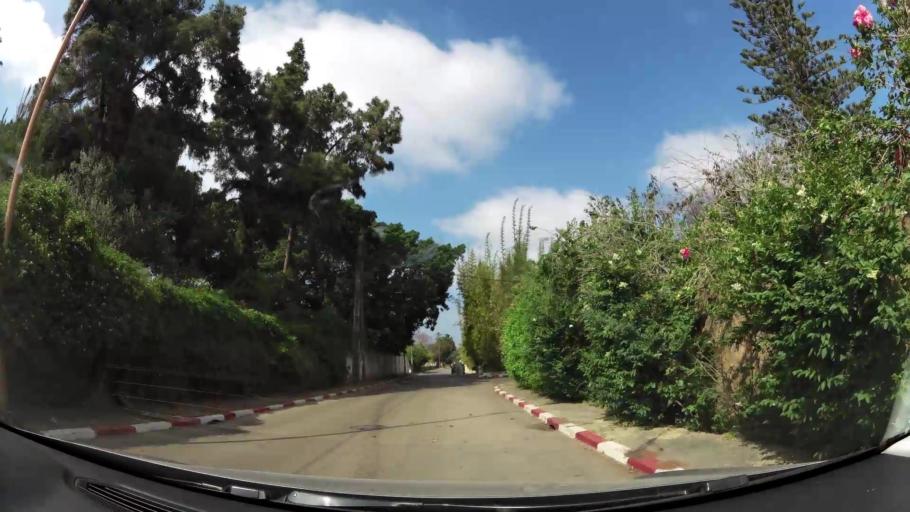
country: MA
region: Rabat-Sale-Zemmour-Zaer
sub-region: Rabat
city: Rabat
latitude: 33.9777
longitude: -6.8444
